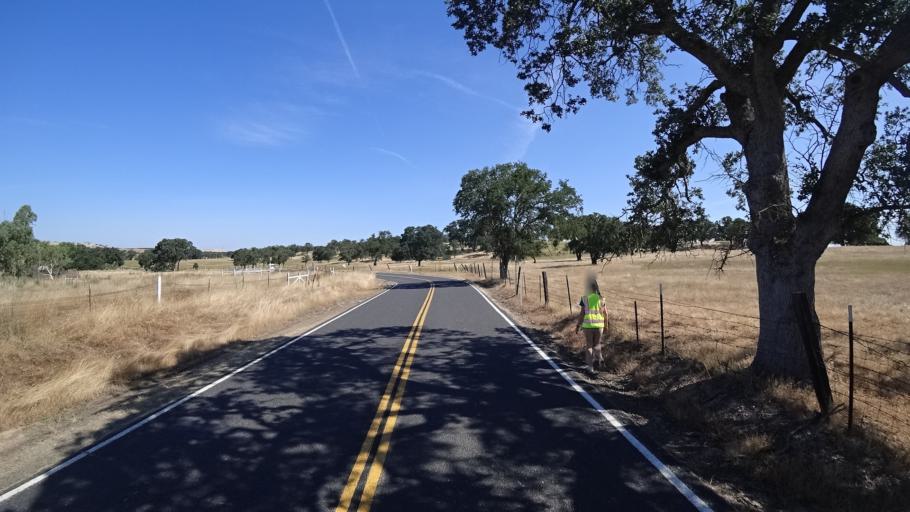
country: US
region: California
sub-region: Calaveras County
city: Rancho Calaveras
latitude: 38.1060
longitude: -120.9224
